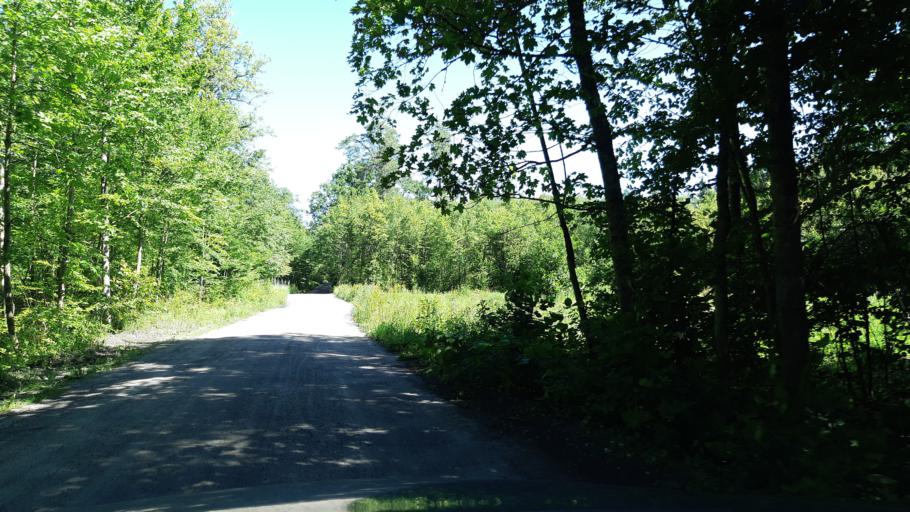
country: PL
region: Warmian-Masurian Voivodeship
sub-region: Powiat piski
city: Ruciane-Nida
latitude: 53.7005
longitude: 21.4729
